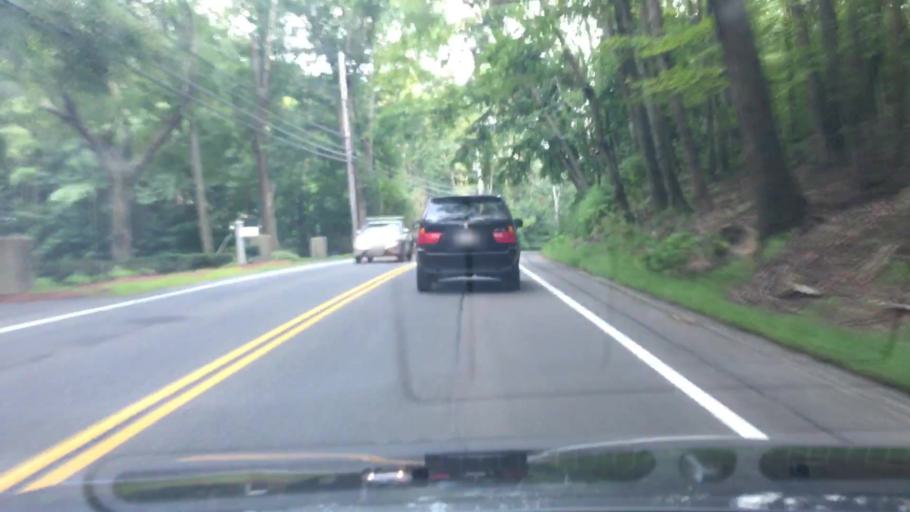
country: US
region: Massachusetts
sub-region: Middlesex County
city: Hopkinton
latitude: 42.2337
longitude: -71.5552
